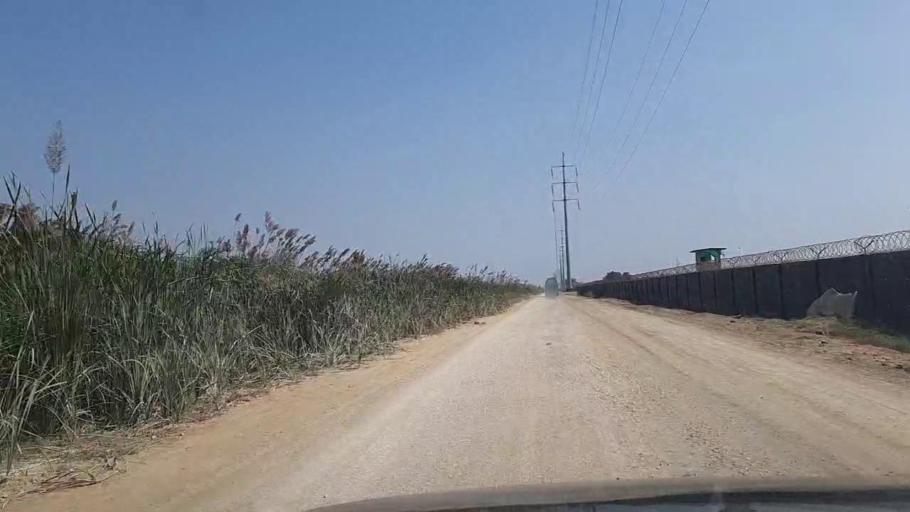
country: PK
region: Sindh
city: Gharo
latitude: 24.7218
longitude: 67.5366
